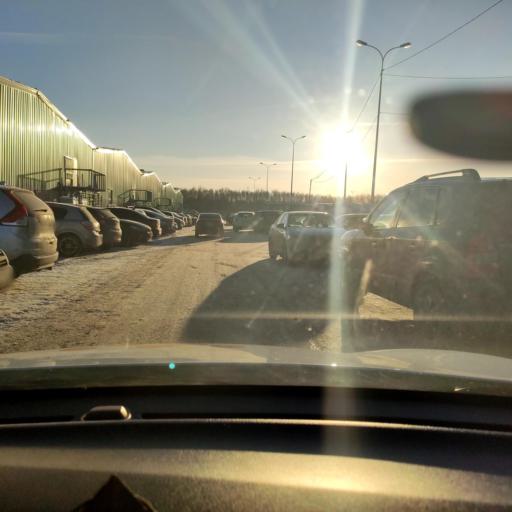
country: RU
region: Tatarstan
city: Osinovo
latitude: 55.8575
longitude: 48.8334
